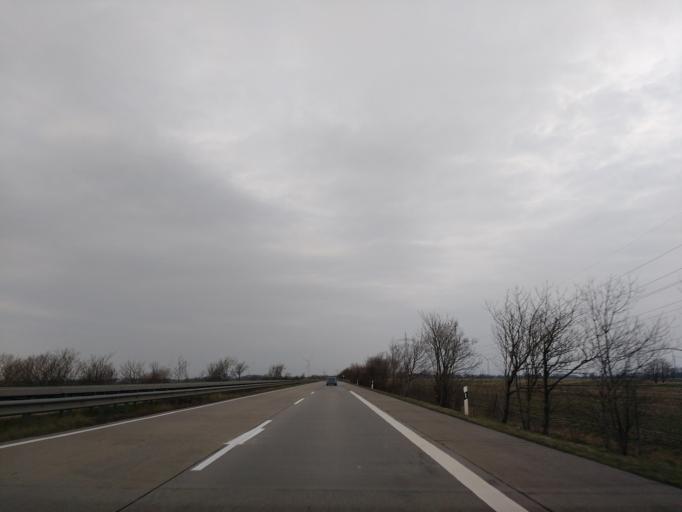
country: DE
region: Lower Saxony
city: Cuxhaven
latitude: 53.7937
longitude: 8.7082
